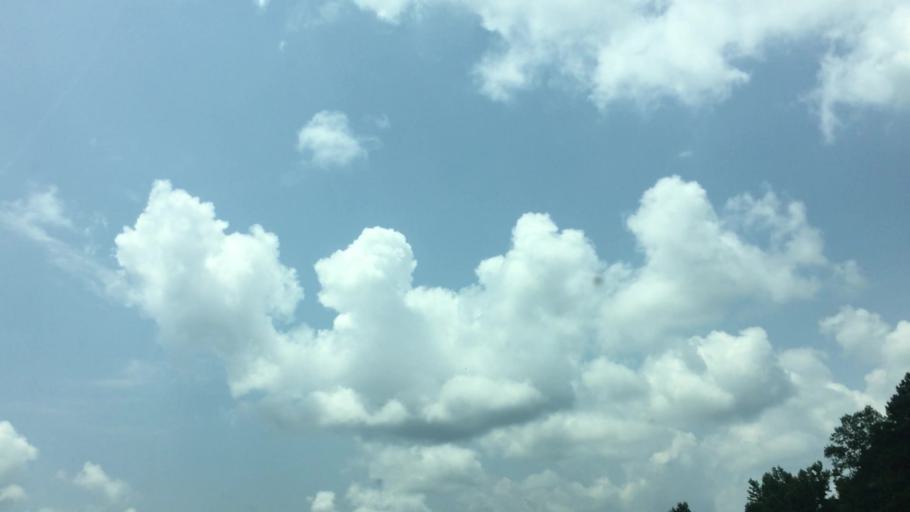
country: US
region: Georgia
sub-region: Fulton County
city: Palmetto
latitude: 33.5677
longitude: -84.7021
